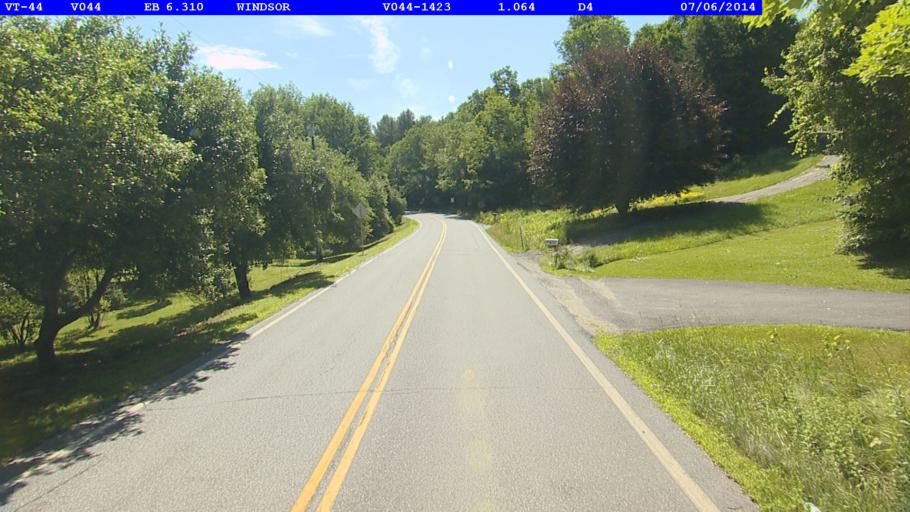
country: US
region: Vermont
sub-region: Windsor County
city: Windsor
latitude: 43.4638
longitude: -72.4328
